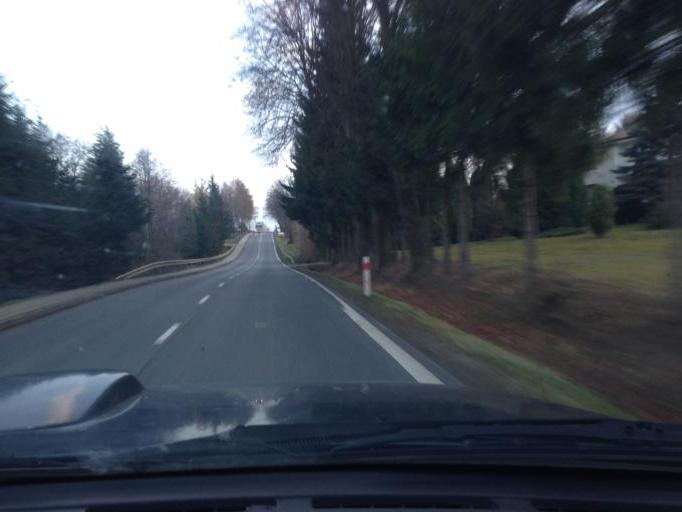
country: PL
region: Subcarpathian Voivodeship
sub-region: Powiat jasielski
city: Osiek Jasielski
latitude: 49.6410
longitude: 21.5195
